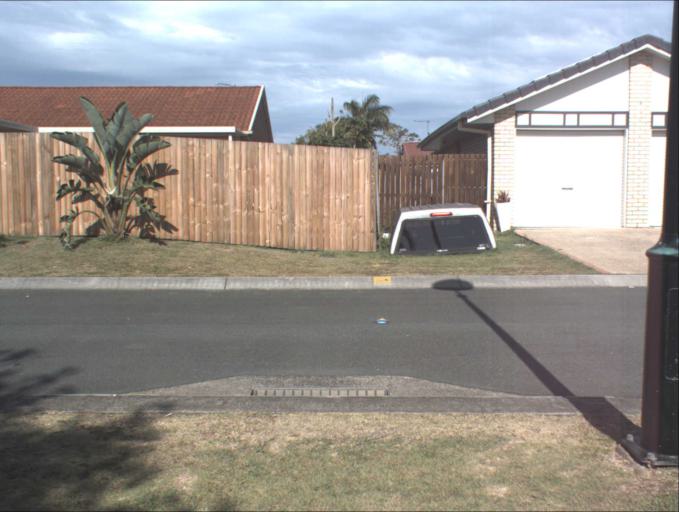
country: AU
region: Queensland
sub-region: Logan
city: Beenleigh
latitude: -27.6749
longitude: 153.2119
